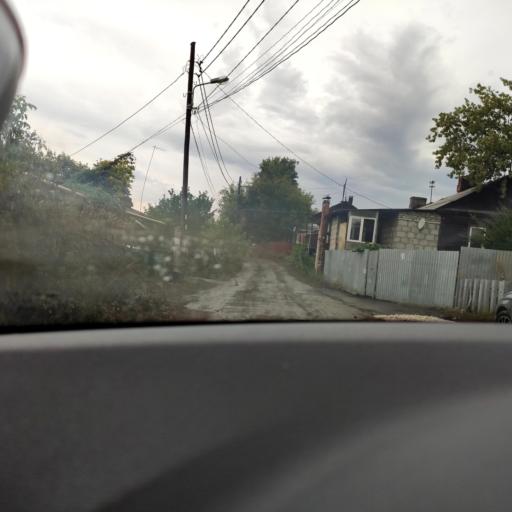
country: RU
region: Samara
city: Samara
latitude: 53.1746
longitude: 50.1556
